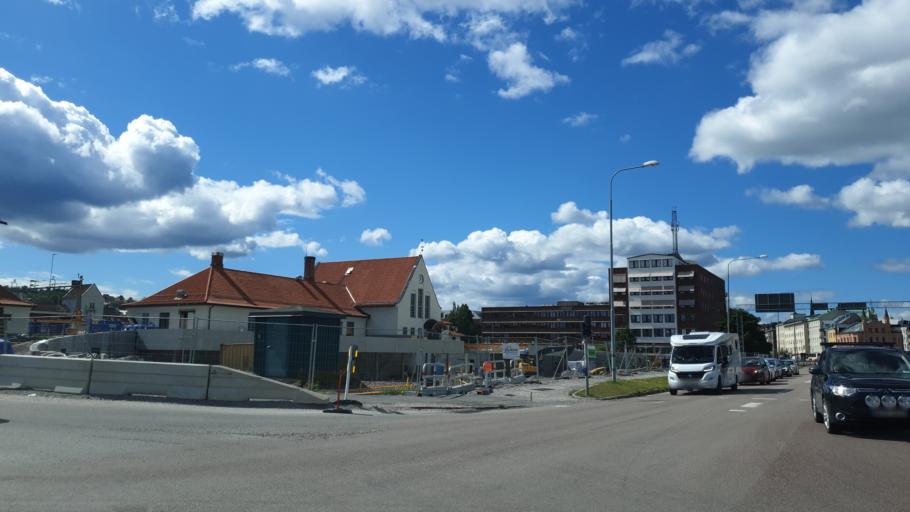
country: SE
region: Vaesternorrland
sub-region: Sundsvalls Kommun
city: Sundsvall
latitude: 62.3871
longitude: 17.3178
